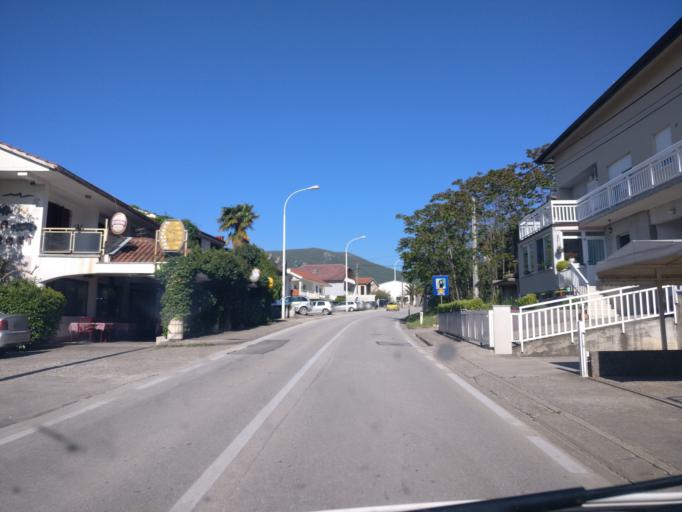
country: BA
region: Federation of Bosnia and Herzegovina
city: Capljina
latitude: 43.1193
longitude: 17.6895
